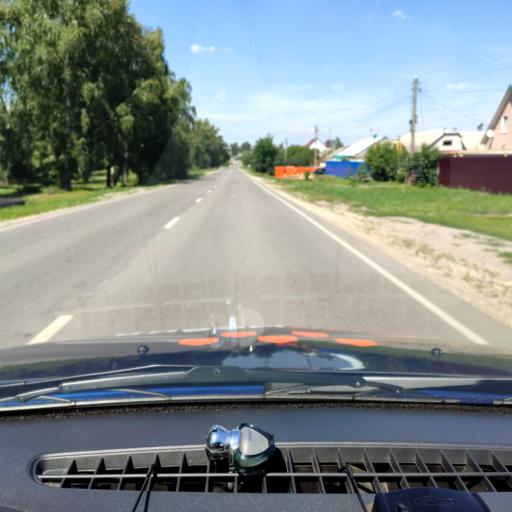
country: RU
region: Voronezj
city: Podgornoye
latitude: 51.8814
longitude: 39.1729
